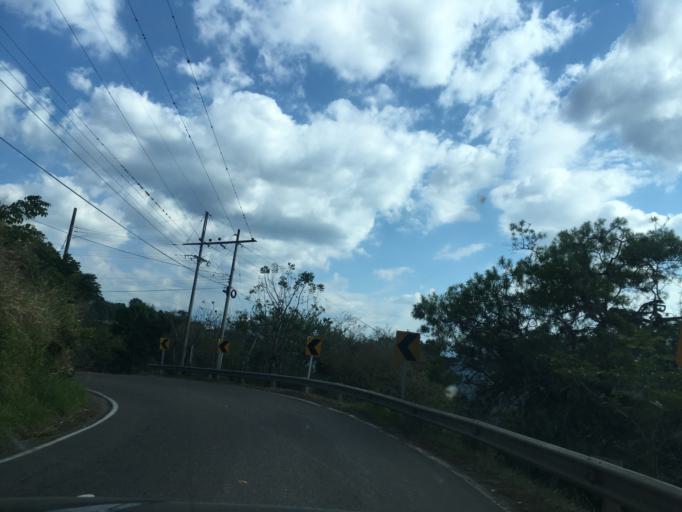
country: CO
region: Santander
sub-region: San Gil
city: San Gil
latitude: 6.5745
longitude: -73.1515
